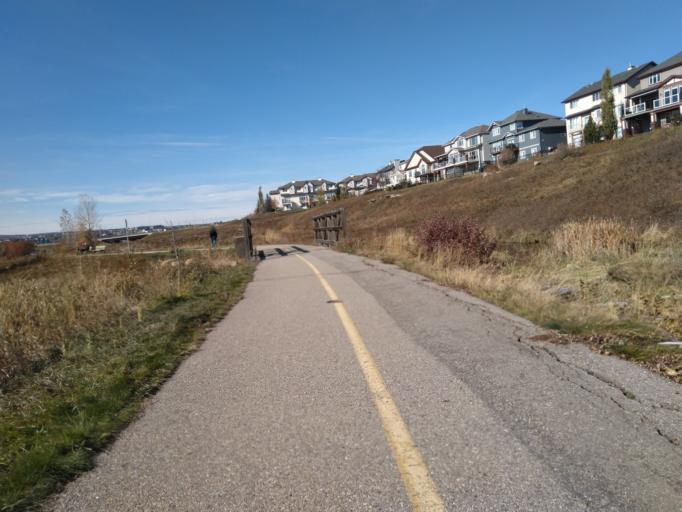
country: CA
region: Alberta
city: Calgary
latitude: 51.1568
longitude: -114.1045
